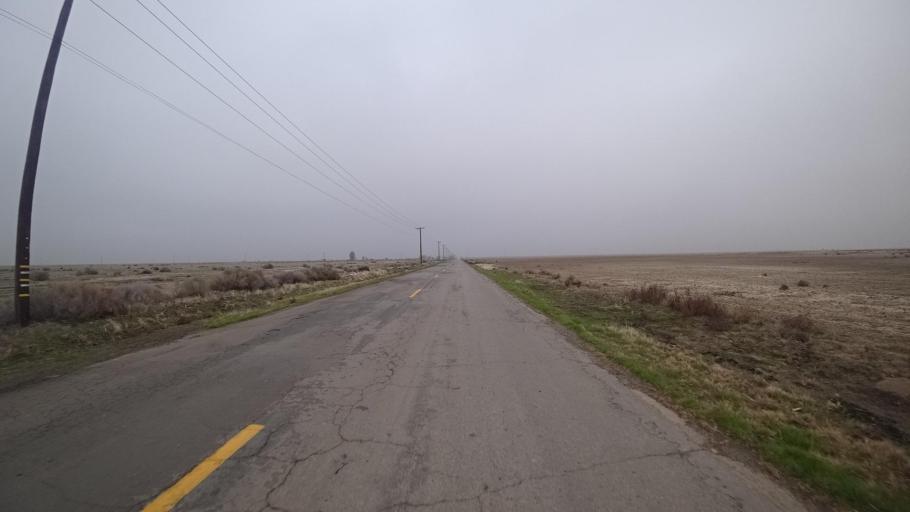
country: US
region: California
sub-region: Tulare County
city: Alpaugh
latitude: 35.7174
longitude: -119.4712
